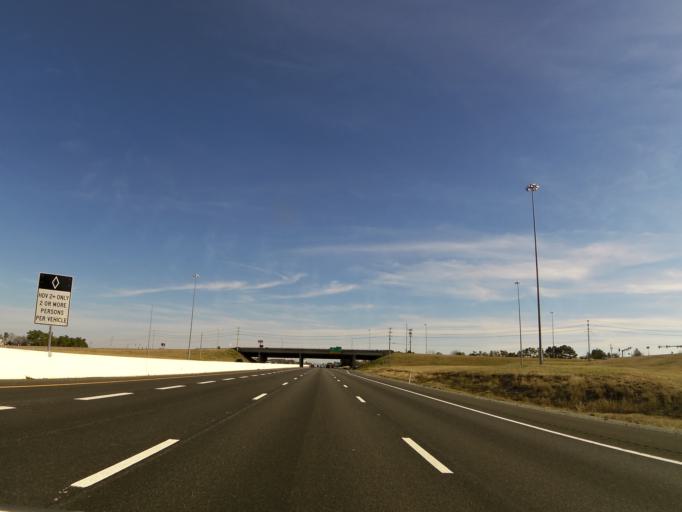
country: US
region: Tennessee
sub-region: Rutherford County
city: Murfreesboro
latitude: 35.8498
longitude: -86.4382
